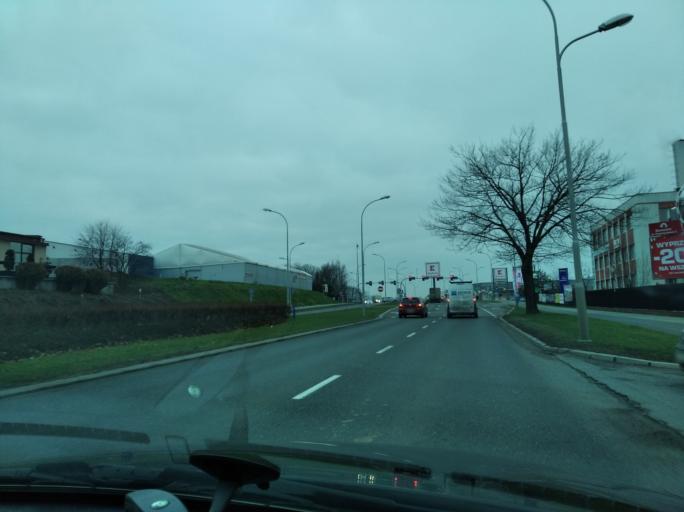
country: PL
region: Subcarpathian Voivodeship
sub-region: Rzeszow
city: Rzeszow
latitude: 50.0490
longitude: 21.9875
